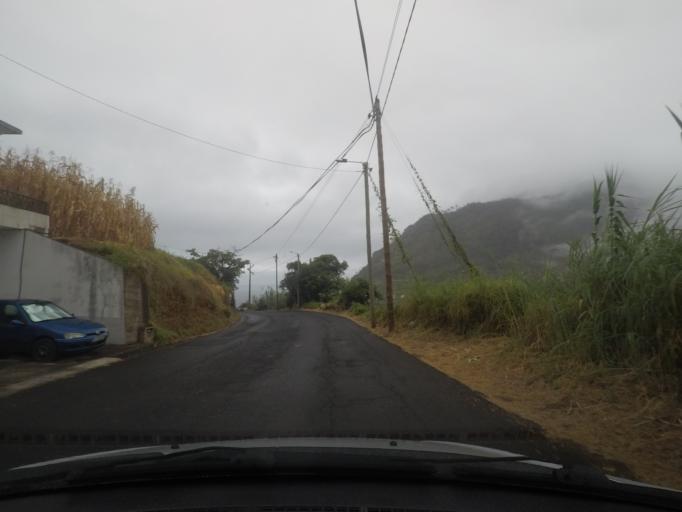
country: PT
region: Madeira
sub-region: Santana
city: Santana
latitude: 32.7868
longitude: -16.8563
